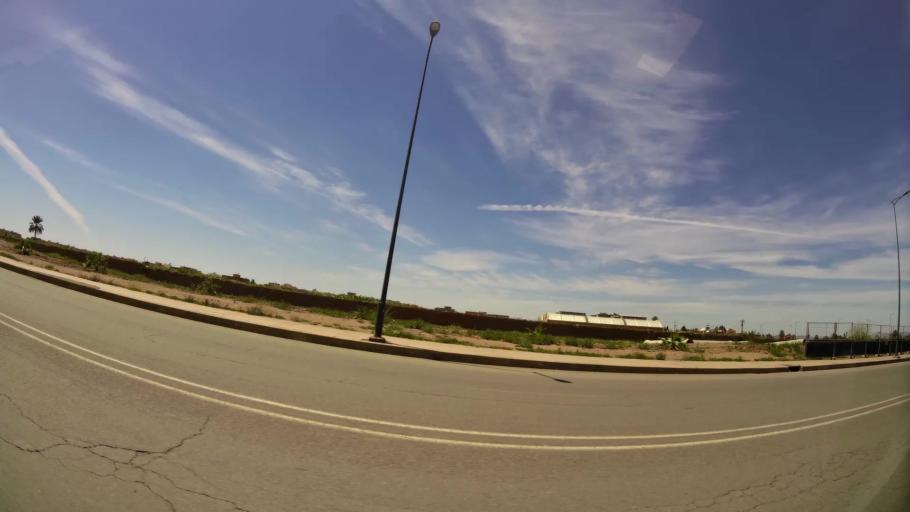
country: MA
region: Marrakech-Tensift-Al Haouz
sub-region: Marrakech
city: Marrakesh
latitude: 31.6524
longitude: -8.0670
